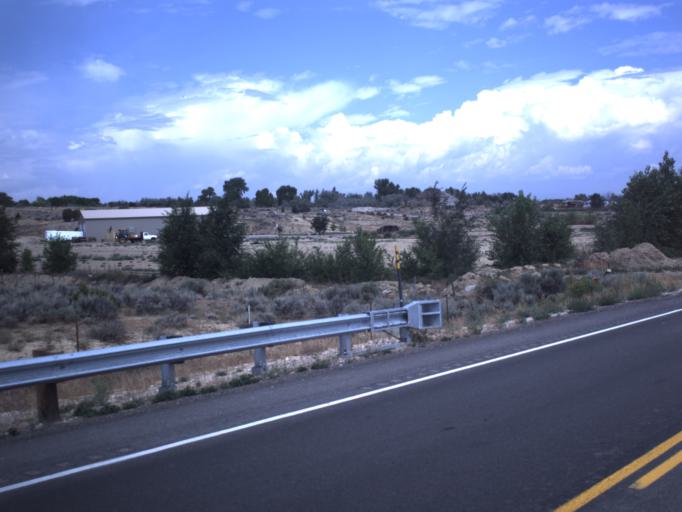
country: US
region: Utah
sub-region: Uintah County
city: Naples
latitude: 40.3641
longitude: -109.4982
